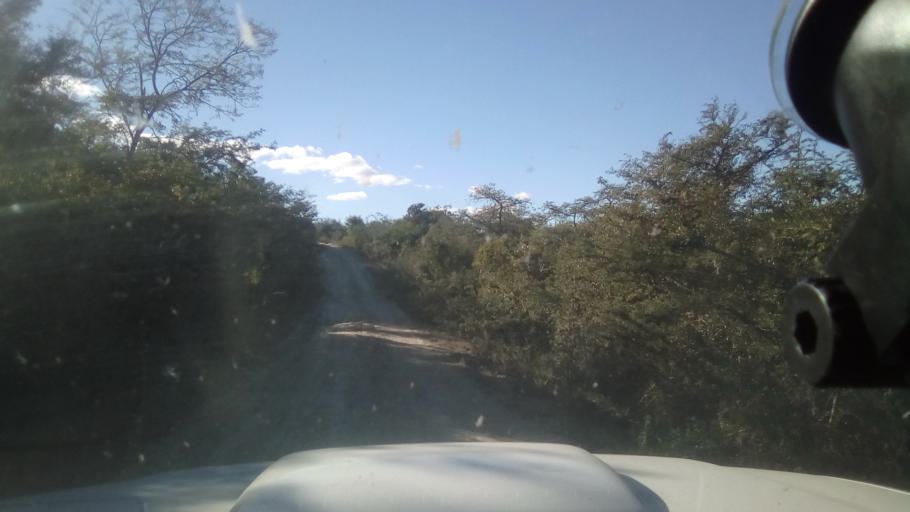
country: ZA
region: Eastern Cape
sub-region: Buffalo City Metropolitan Municipality
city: Bhisho
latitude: -32.7381
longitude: 27.3481
